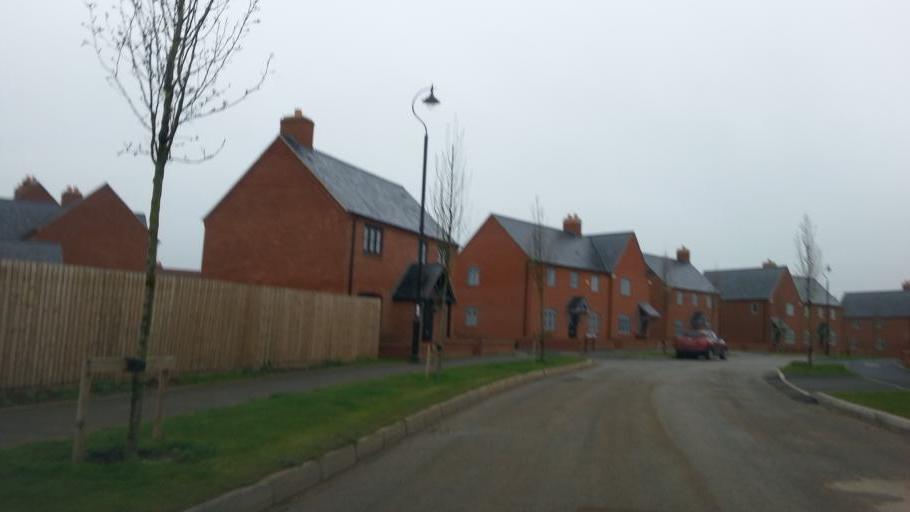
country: GB
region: England
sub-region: Northamptonshire
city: Brackley
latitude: 52.0452
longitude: -1.1500
